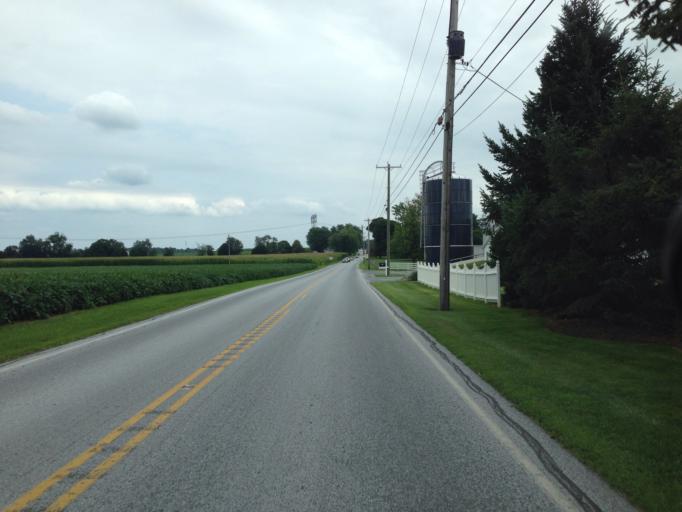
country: US
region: Pennsylvania
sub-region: Chester County
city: Oxford
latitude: 39.8555
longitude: -75.9706
